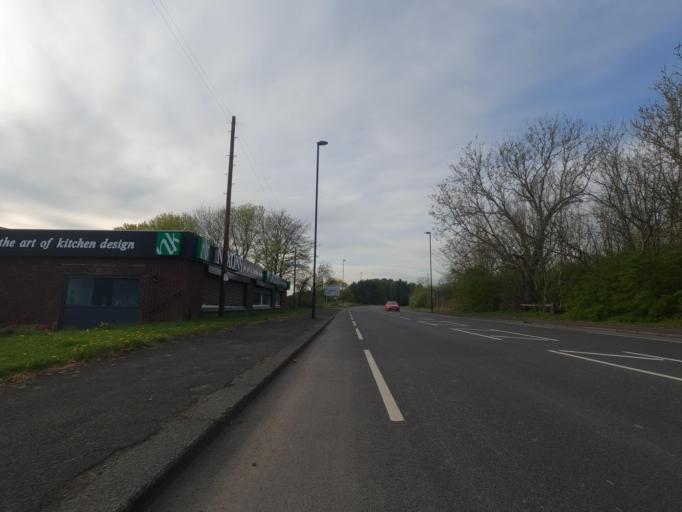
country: GB
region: England
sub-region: Newcastle upon Tyne
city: Hazlerigg
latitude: 55.0628
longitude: -1.6316
